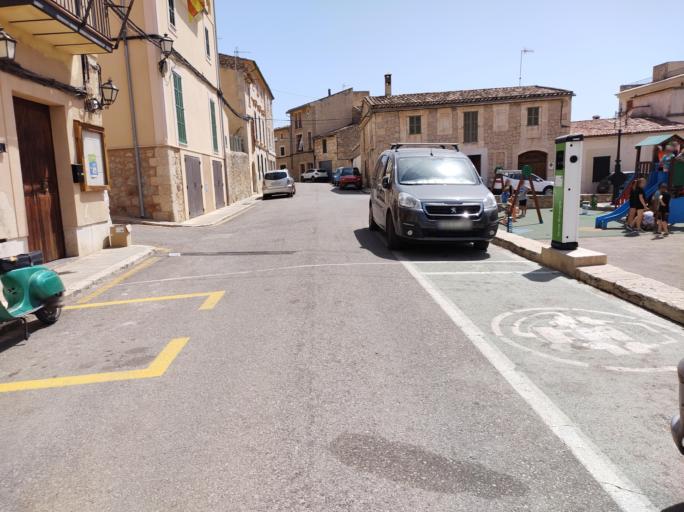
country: ES
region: Balearic Islands
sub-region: Illes Balears
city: Selva
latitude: 39.7712
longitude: 2.9034
